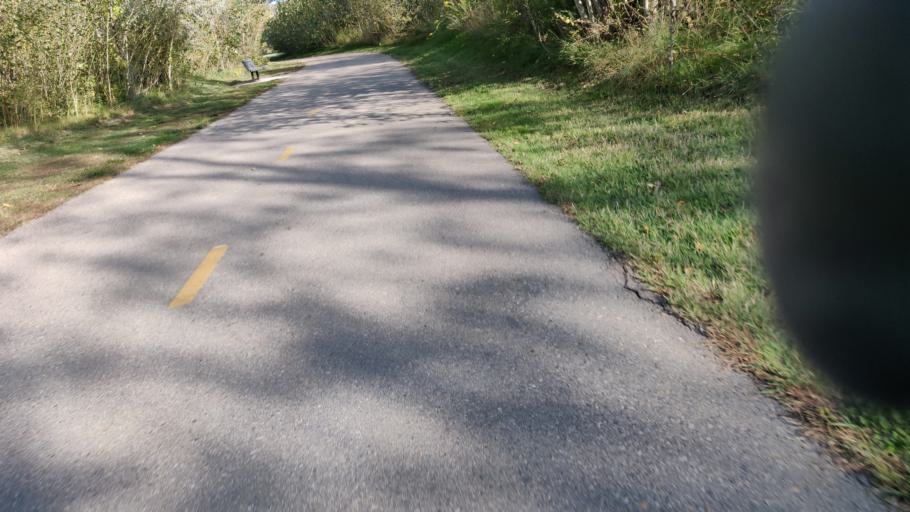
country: US
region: Idaho
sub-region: Ada County
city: Boise
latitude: 43.5753
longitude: -116.1491
